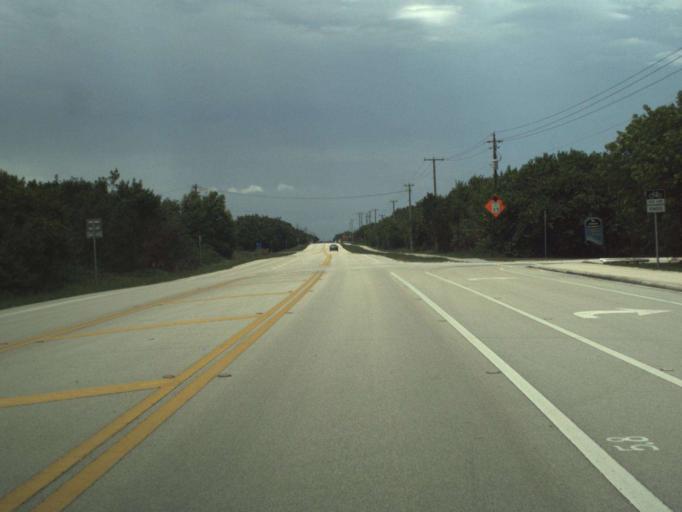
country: US
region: Florida
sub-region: Saint Lucie County
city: Hutchinson Island South
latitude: 27.3403
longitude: -80.2374
